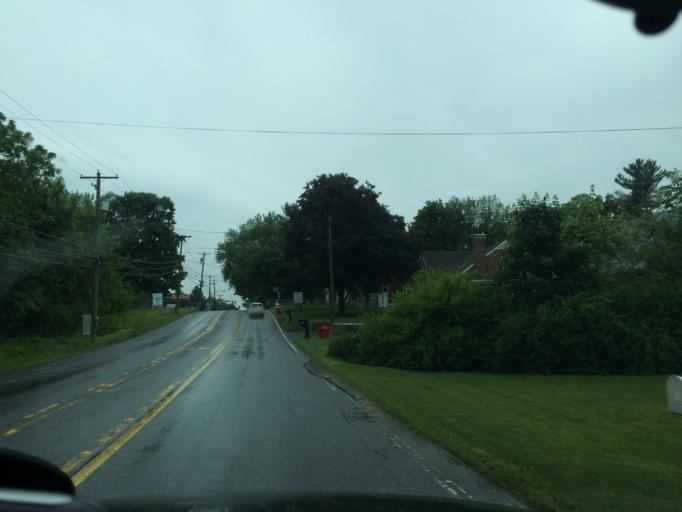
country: US
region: Maryland
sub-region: Washington County
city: Robinwood
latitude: 39.6428
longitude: -77.6522
